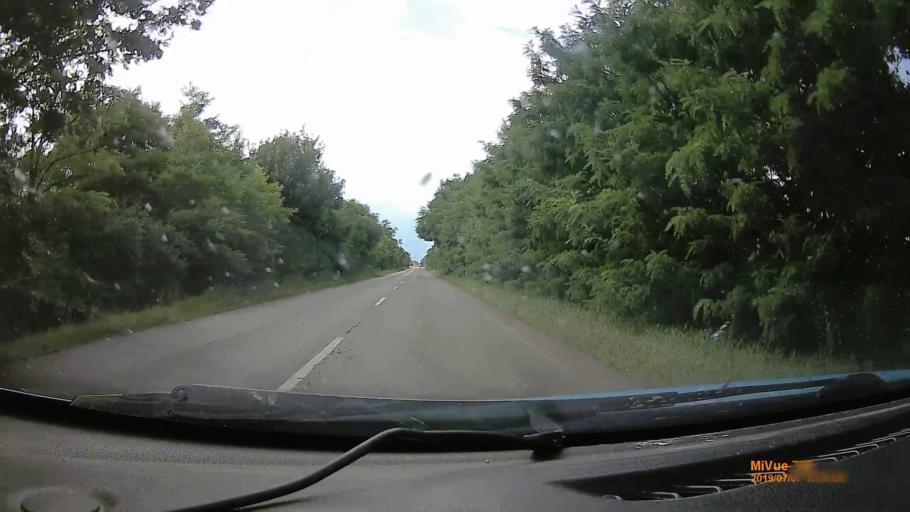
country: HU
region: Pest
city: Szentlorinckata
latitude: 47.5490
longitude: 19.8060
